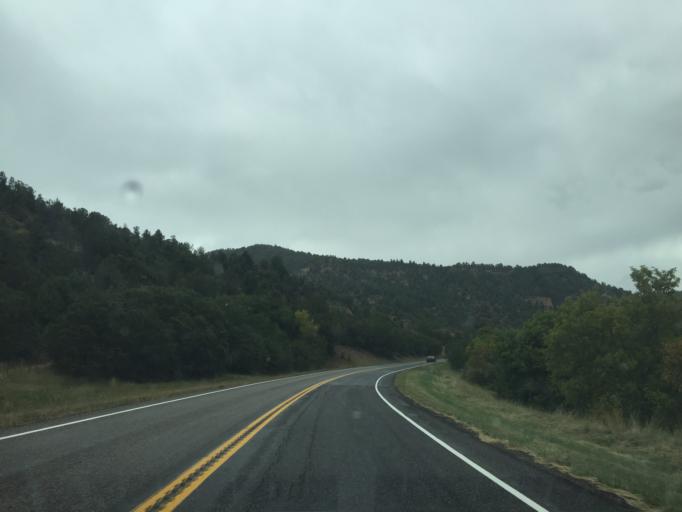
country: US
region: Utah
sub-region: Kane County
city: Kanab
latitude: 37.3566
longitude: -112.5993
